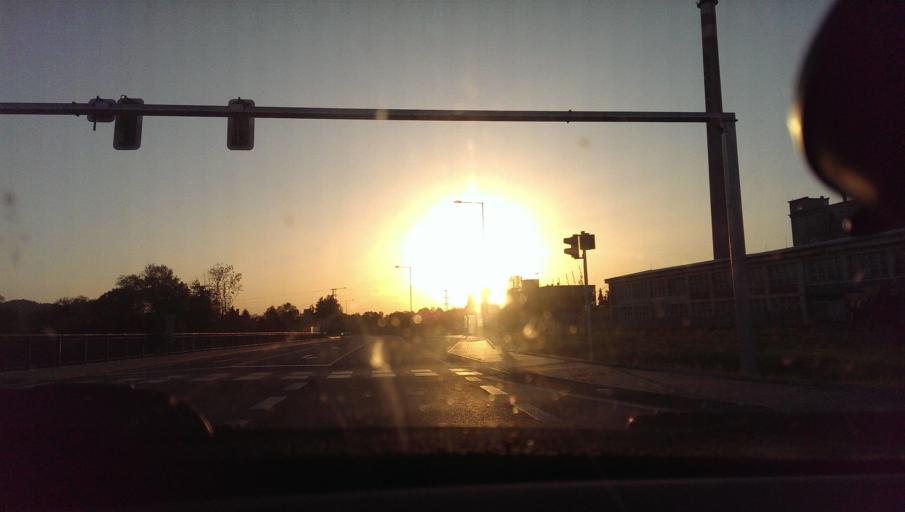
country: CZ
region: Zlin
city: Zubri
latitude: 49.4611
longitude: 18.0923
